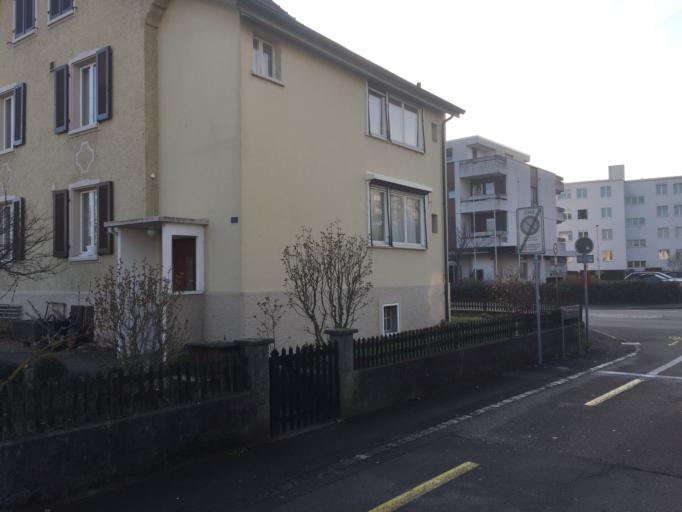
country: CH
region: Aargau
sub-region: Bezirk Rheinfelden
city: Kaiseraugst
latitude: 47.5343
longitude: 7.7135
